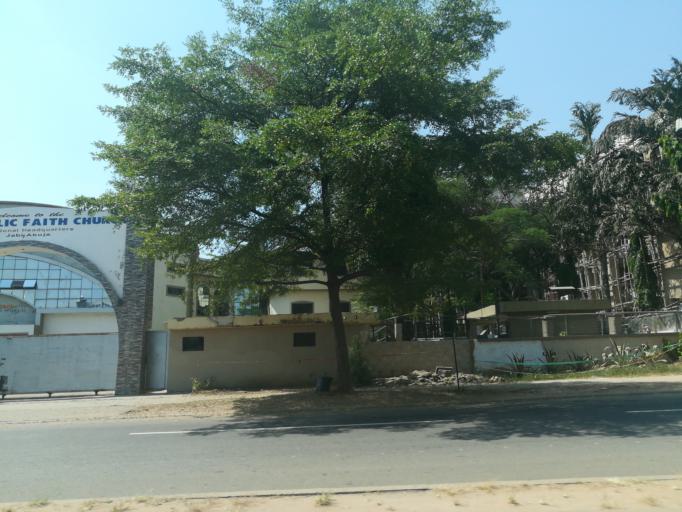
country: NG
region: Abuja Federal Capital Territory
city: Abuja
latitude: 9.0623
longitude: 7.4223
